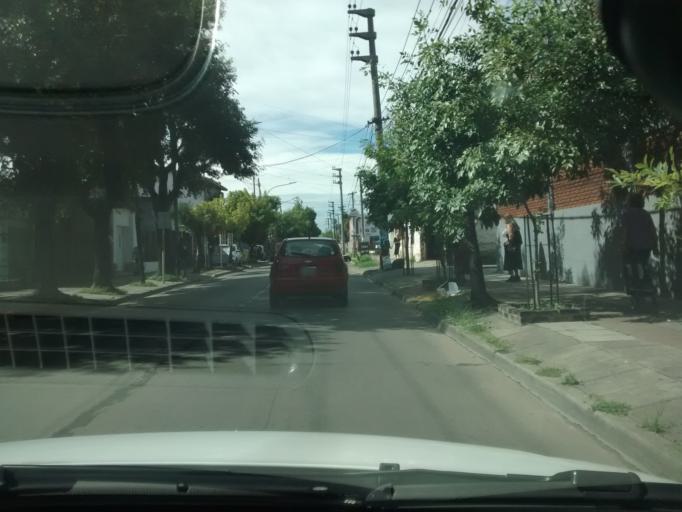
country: AR
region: Buenos Aires
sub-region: Partido de Moron
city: Moron
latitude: -34.6655
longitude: -58.6174
